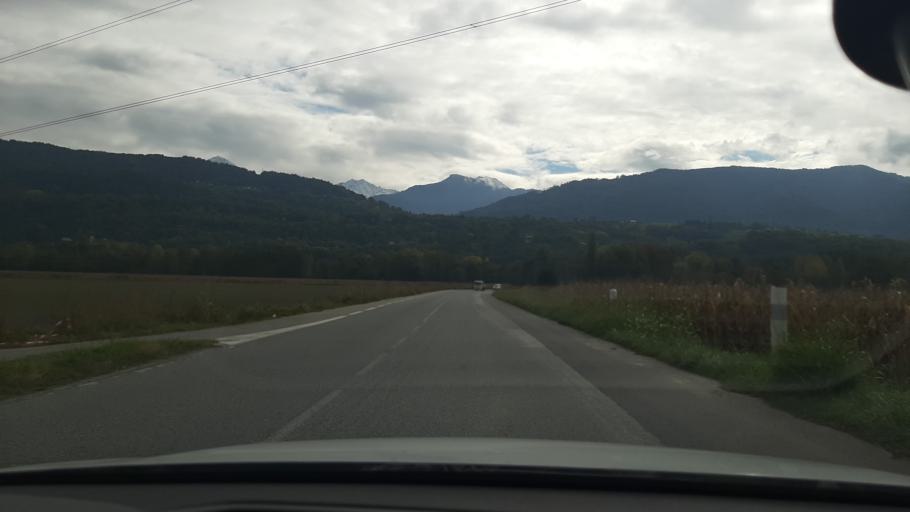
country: FR
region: Rhone-Alpes
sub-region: Departement de la Savoie
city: Montmelian
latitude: 45.4669
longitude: 6.0440
